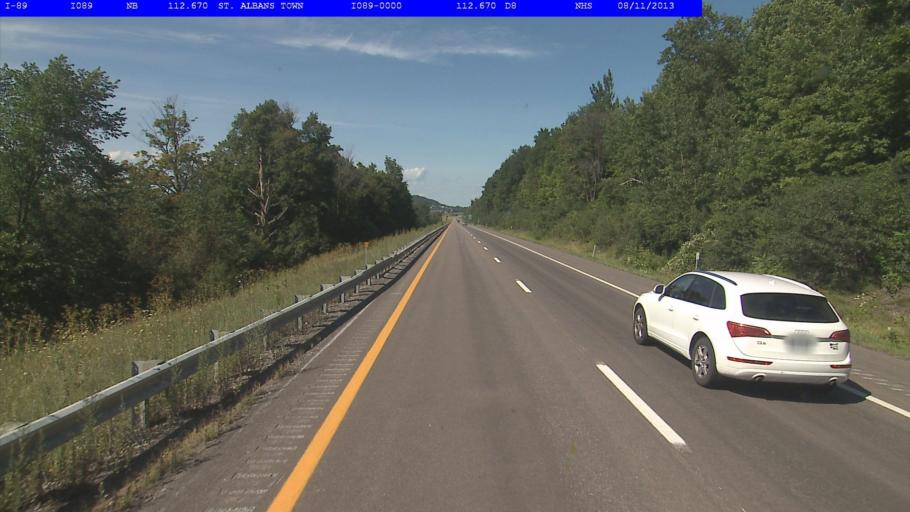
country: US
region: Vermont
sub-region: Franklin County
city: Saint Albans
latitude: 44.7796
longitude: -73.0734
